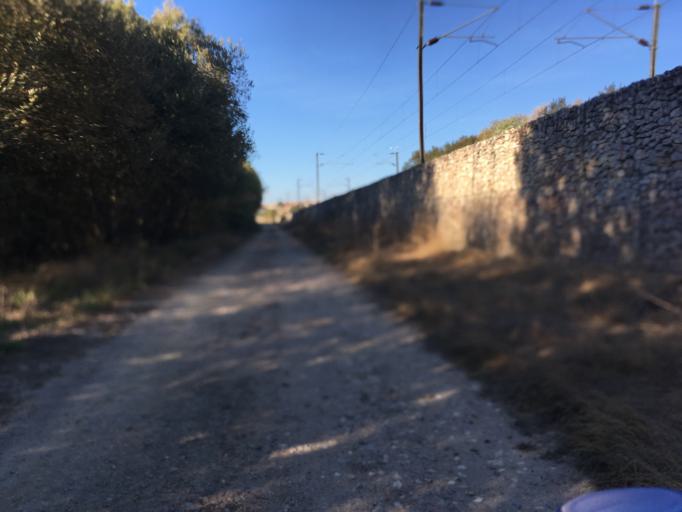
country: PT
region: Aveiro
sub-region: Estarreja
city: Salreu
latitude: 40.7226
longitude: -8.5644
